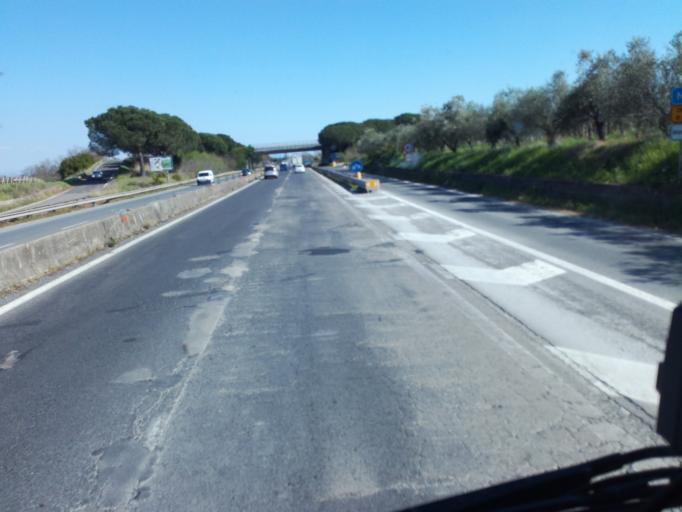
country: IT
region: Latium
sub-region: Provincia di Latina
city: Genio Civile
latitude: 41.5219
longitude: 12.7697
